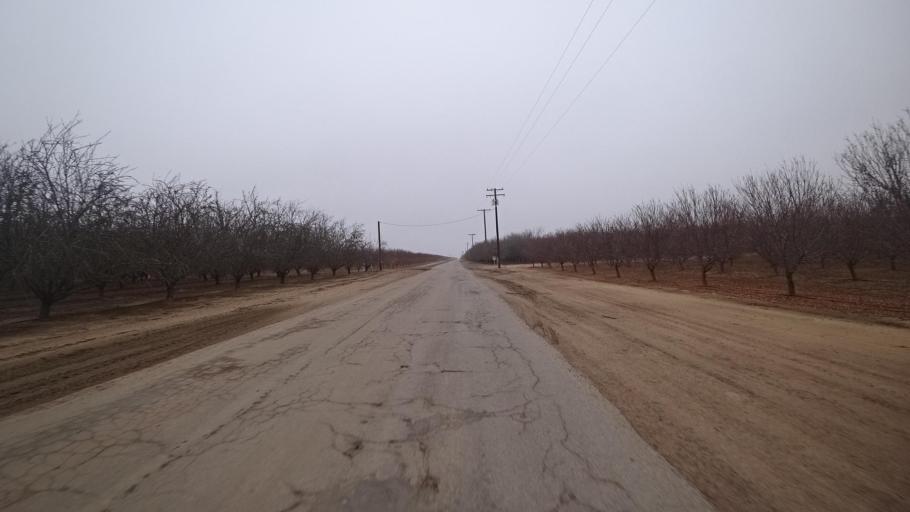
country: US
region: California
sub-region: Kern County
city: Wasco
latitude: 35.5642
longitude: -119.4919
